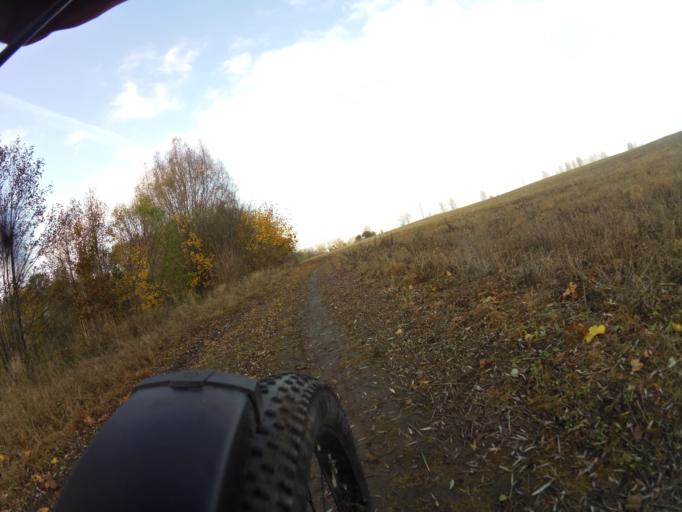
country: PL
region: Pomeranian Voivodeship
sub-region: Powiat pucki
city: Krokowa
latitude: 54.7727
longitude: 18.1705
